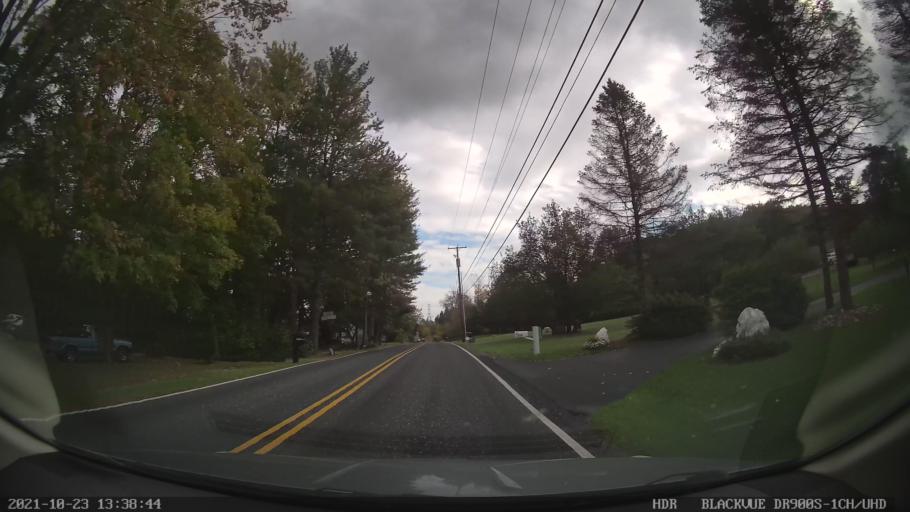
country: US
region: Pennsylvania
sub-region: Berks County
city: Bally
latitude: 40.4313
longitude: -75.5807
